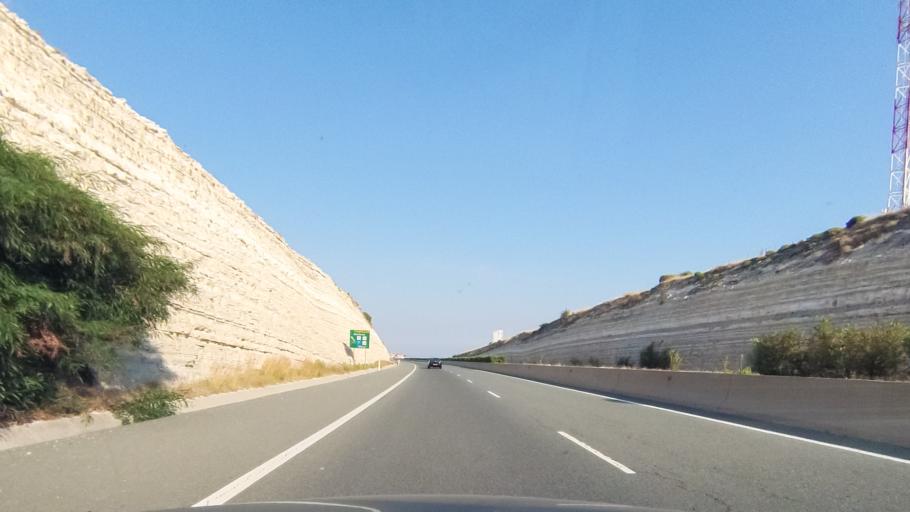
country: CY
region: Limassol
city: Sotira
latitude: 34.6858
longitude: 32.8766
